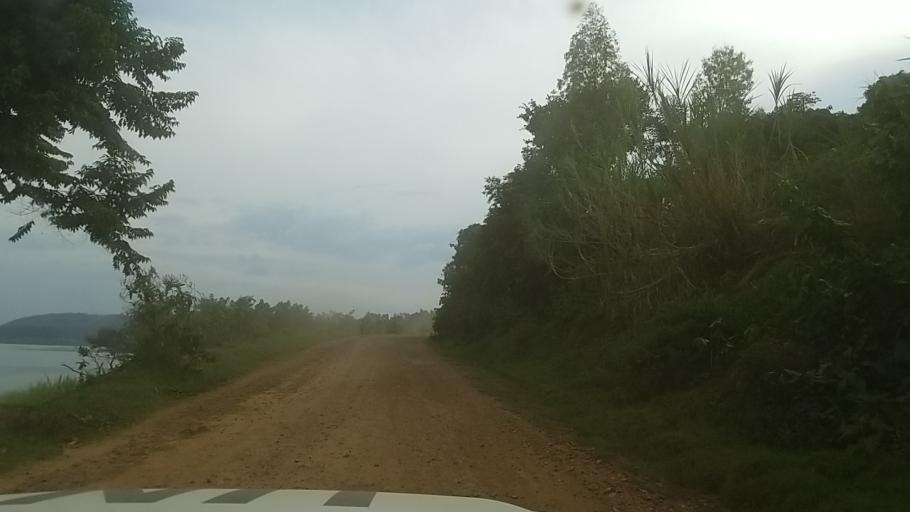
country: RW
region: Western Province
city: Cyangugu
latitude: -2.1058
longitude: 28.9077
